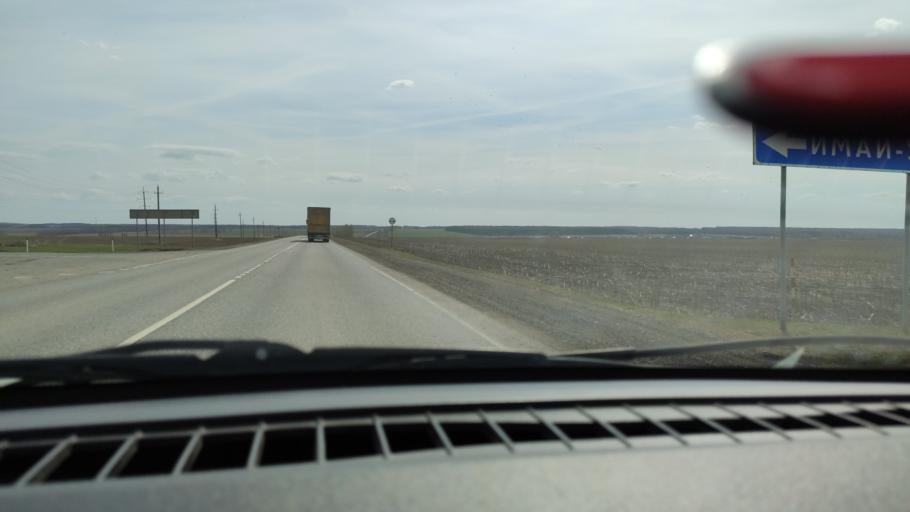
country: RU
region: Bashkortostan
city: Dyurtyuli
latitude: 55.3089
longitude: 54.9995
